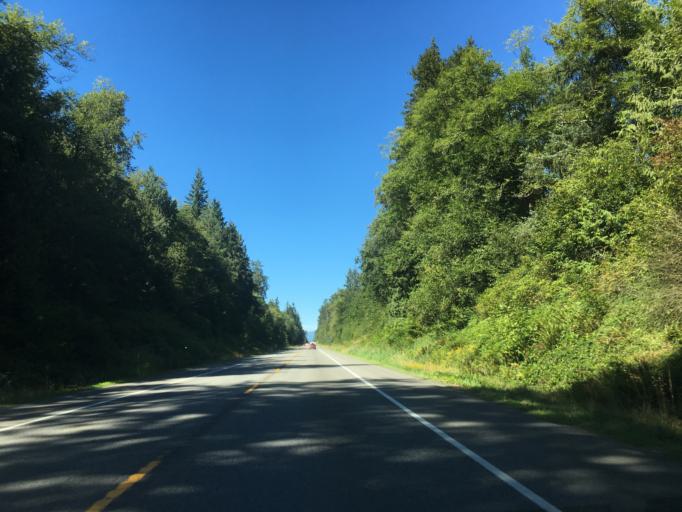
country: US
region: Washington
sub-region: Snohomish County
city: Sisco Heights
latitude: 48.1056
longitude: -122.1121
